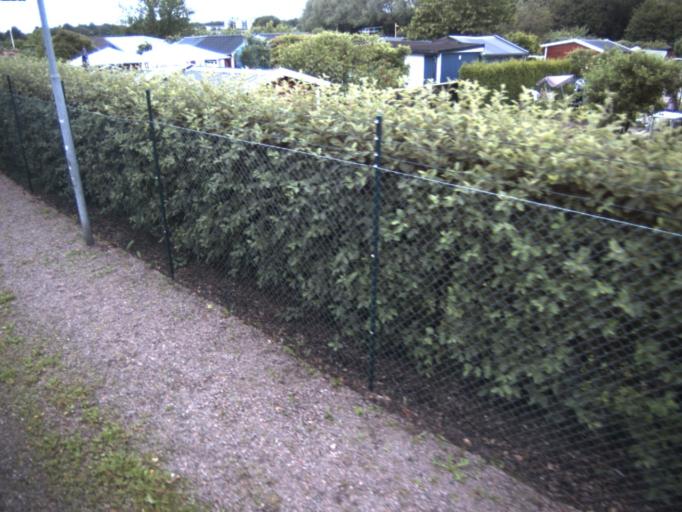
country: SE
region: Skane
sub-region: Helsingborg
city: Helsingborg
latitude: 56.0576
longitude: 12.7317
